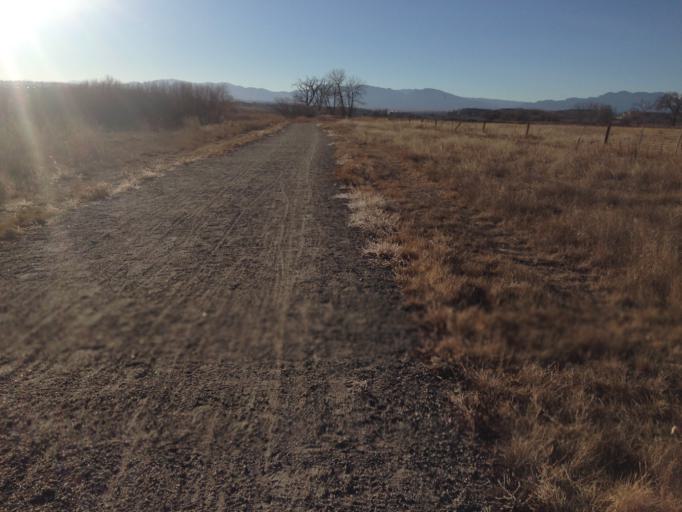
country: US
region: Colorado
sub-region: Broomfield County
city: Broomfield
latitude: 39.9426
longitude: -105.1060
